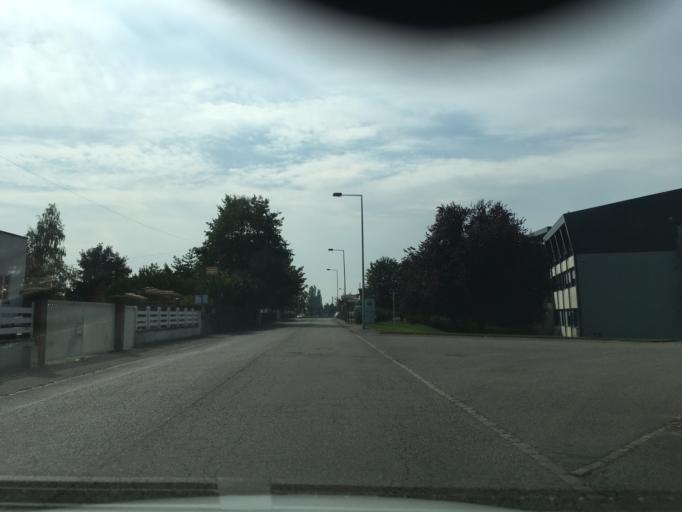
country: FR
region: Alsace
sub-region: Departement du Haut-Rhin
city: Colmar
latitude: 48.0911
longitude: 7.3764
